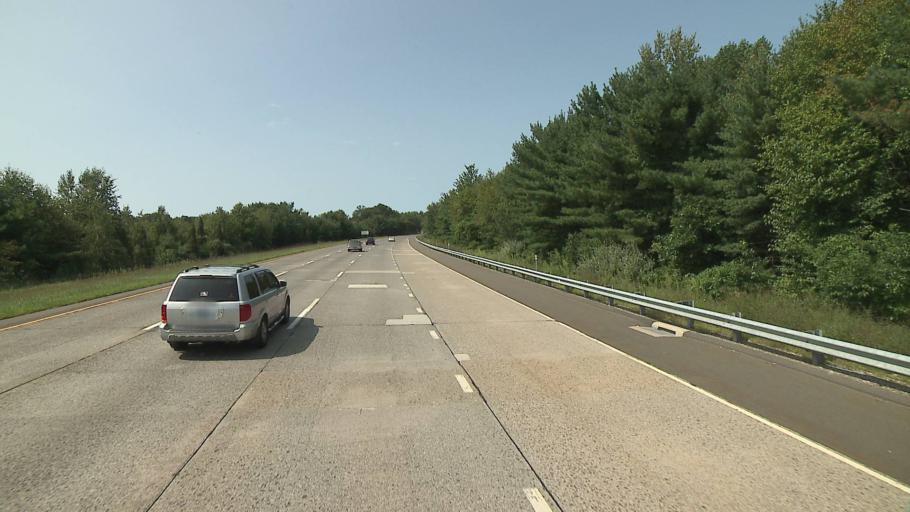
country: US
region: Connecticut
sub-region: Fairfield County
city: Trumbull
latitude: 41.2561
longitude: -73.2035
